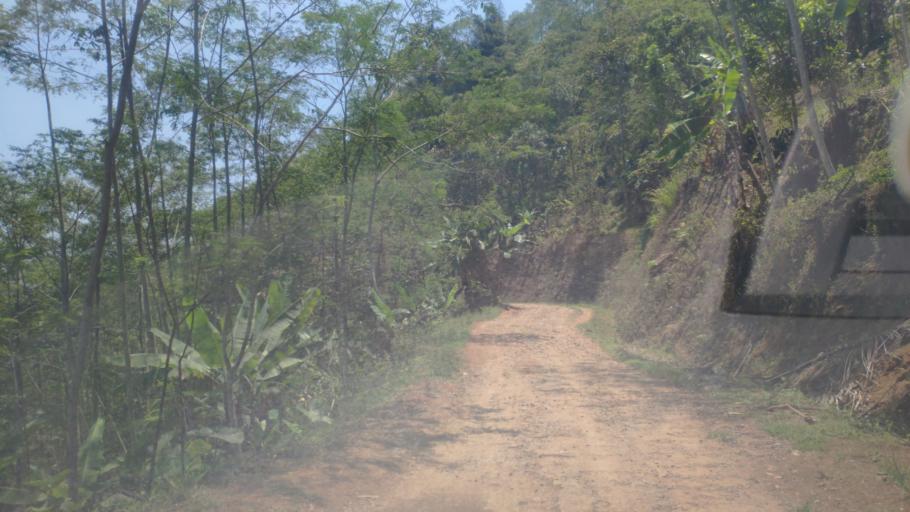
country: ID
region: Central Java
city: Buaran
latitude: -7.2798
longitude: 109.5875
